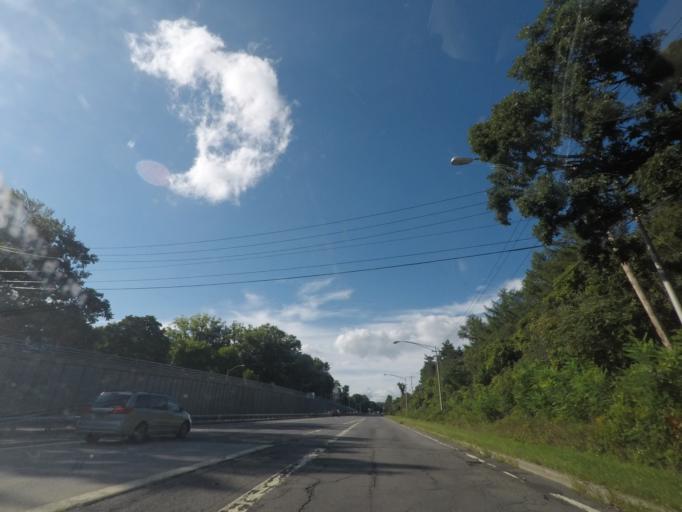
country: US
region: New York
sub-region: Albany County
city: Albany
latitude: 42.6777
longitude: -73.7484
